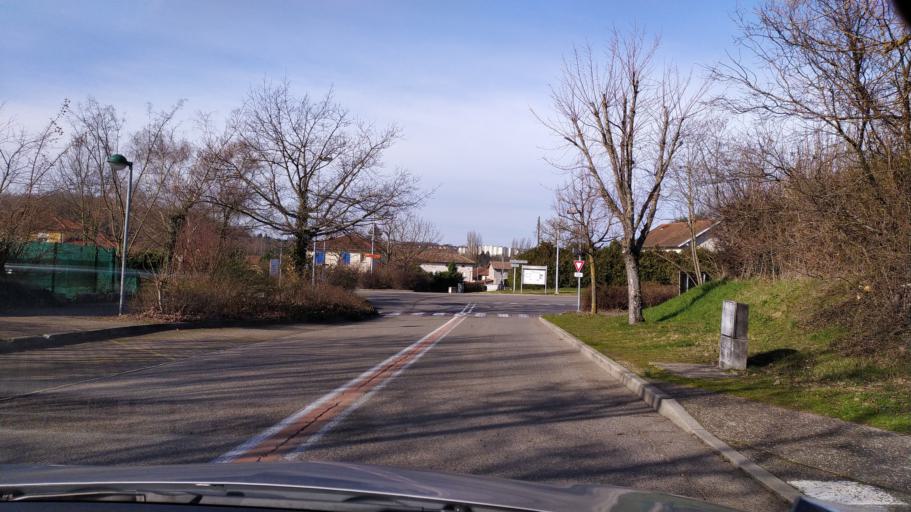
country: FR
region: Rhone-Alpes
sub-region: Departement de l'Isere
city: Vaulx-Milieu
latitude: 45.6035
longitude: 5.1693
